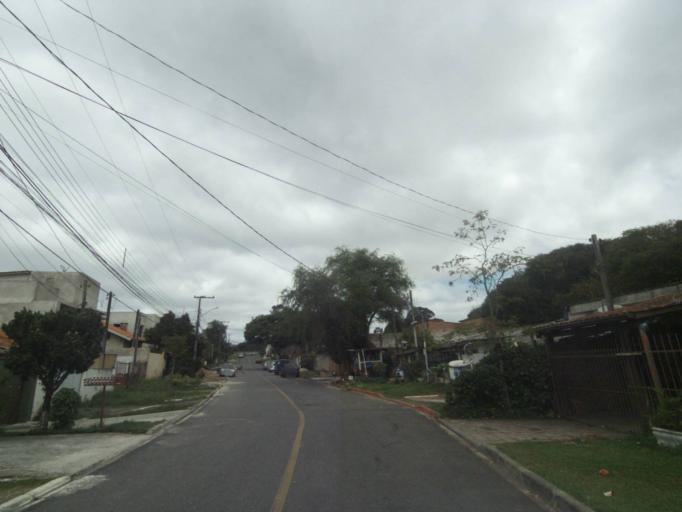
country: BR
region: Parana
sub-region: Pinhais
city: Pinhais
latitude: -25.4047
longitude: -49.2231
